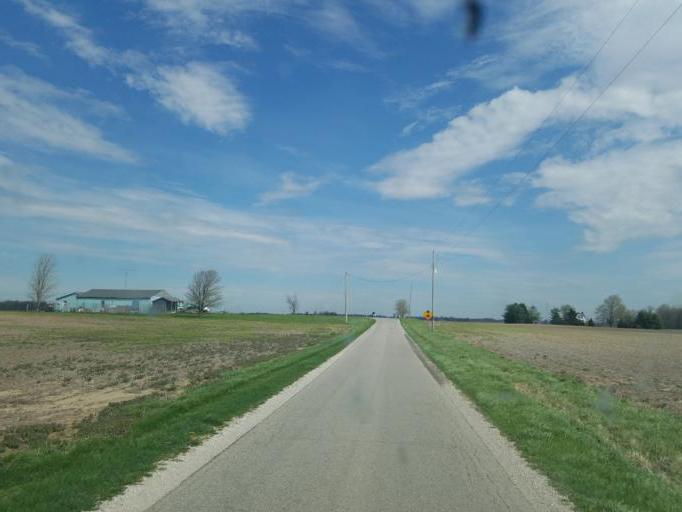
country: US
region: Ohio
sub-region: Crawford County
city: Bucyrus
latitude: 40.7886
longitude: -83.0735
